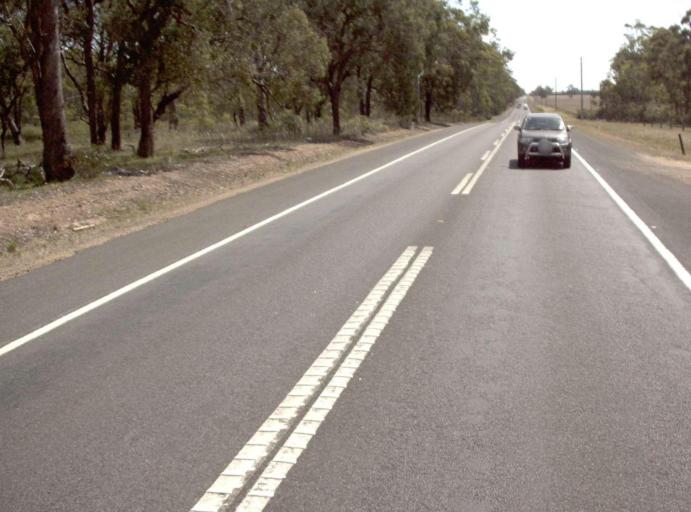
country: AU
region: Victoria
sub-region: Wellington
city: Sale
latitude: -37.9223
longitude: 147.2452
